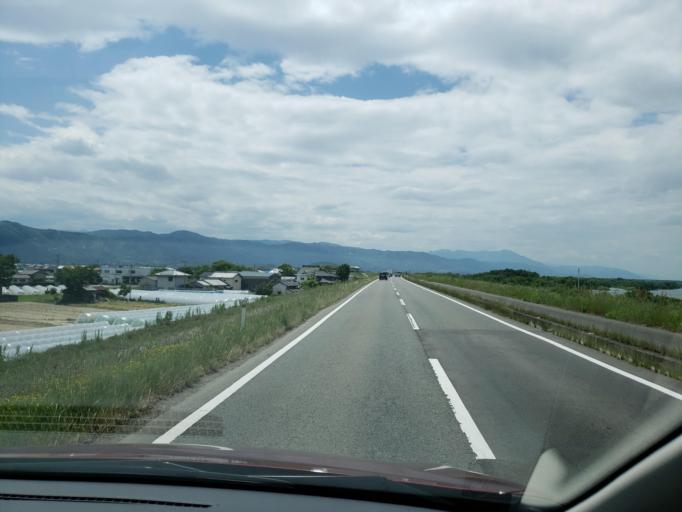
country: JP
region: Tokushima
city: Ishii
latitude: 34.0963
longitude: 134.4214
